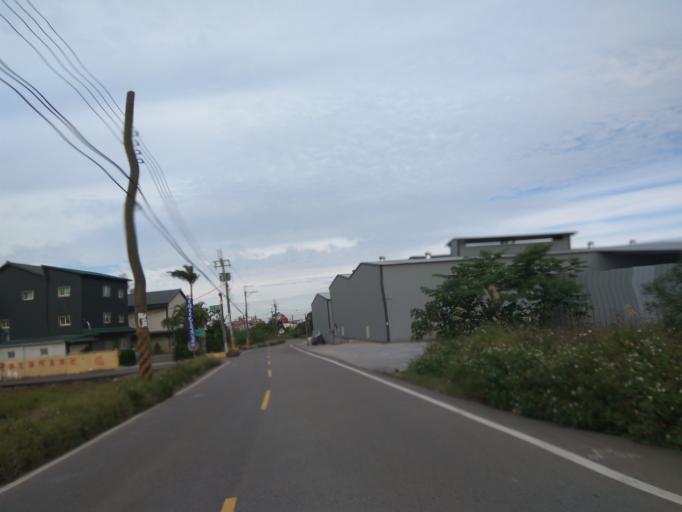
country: TW
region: Taiwan
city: Taoyuan City
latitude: 24.9478
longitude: 121.1435
